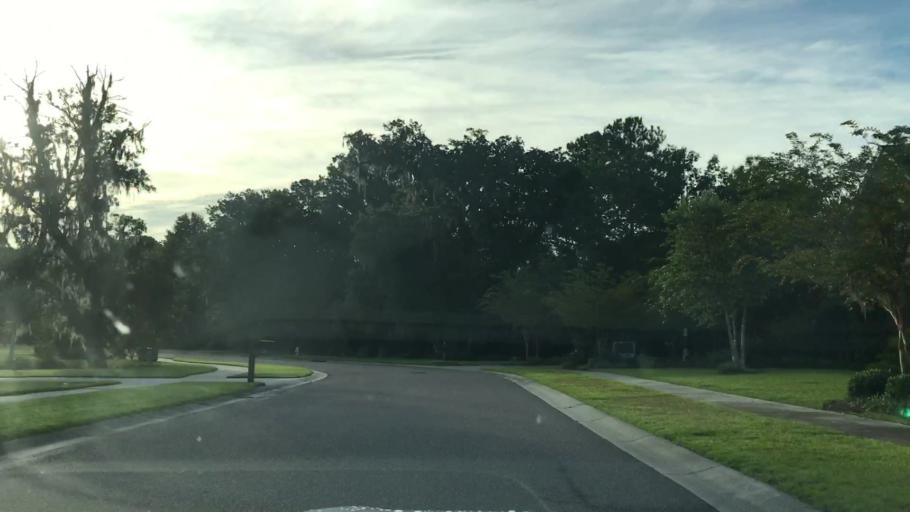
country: US
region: South Carolina
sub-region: Charleston County
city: Shell Point
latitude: 32.8385
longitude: -80.0798
